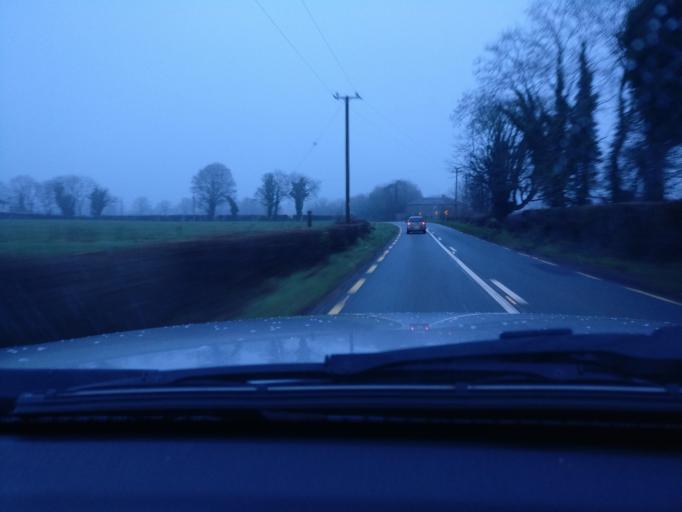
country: IE
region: Leinster
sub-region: An Mhi
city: Athboy
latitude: 53.6415
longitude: -6.8817
